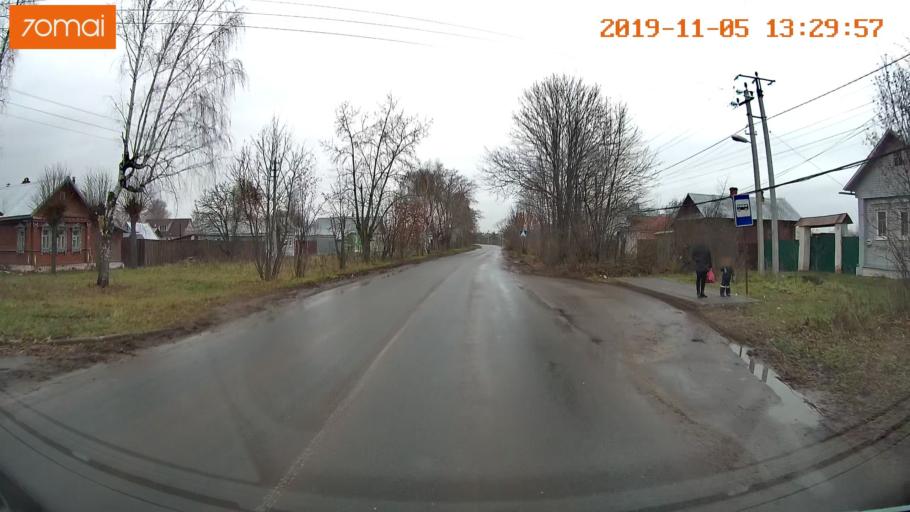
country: RU
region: Ivanovo
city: Shuya
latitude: 56.8638
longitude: 41.3970
